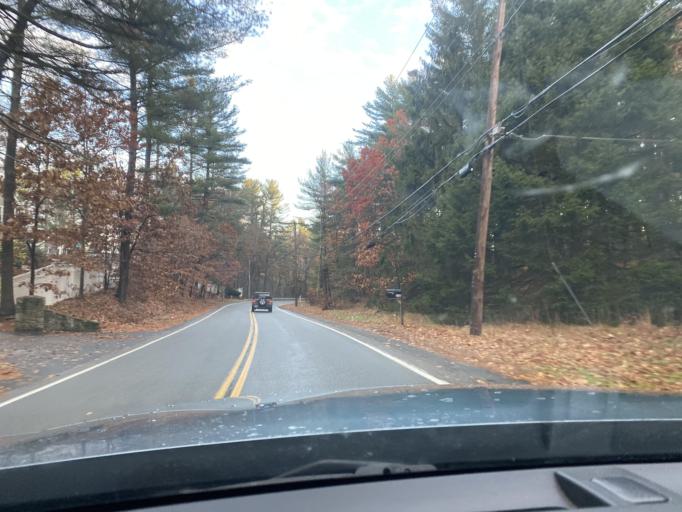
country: US
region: Massachusetts
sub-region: Norfolk County
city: Dover
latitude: 42.2510
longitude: -71.2643
